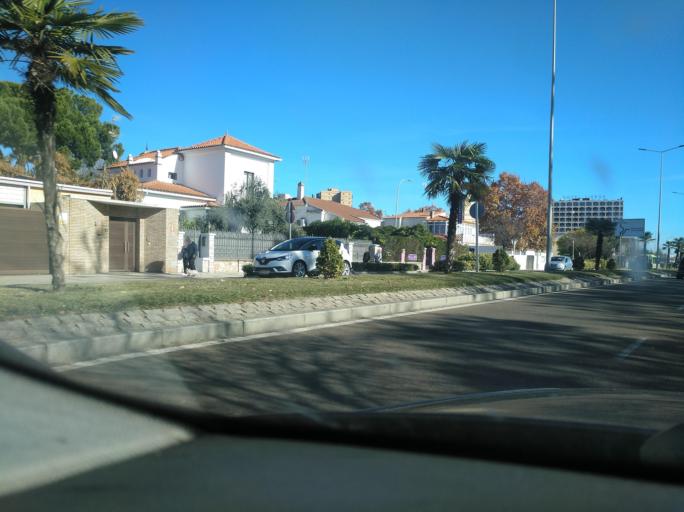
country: ES
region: Extremadura
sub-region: Provincia de Badajoz
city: Badajoz
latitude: 38.8834
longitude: -6.9886
